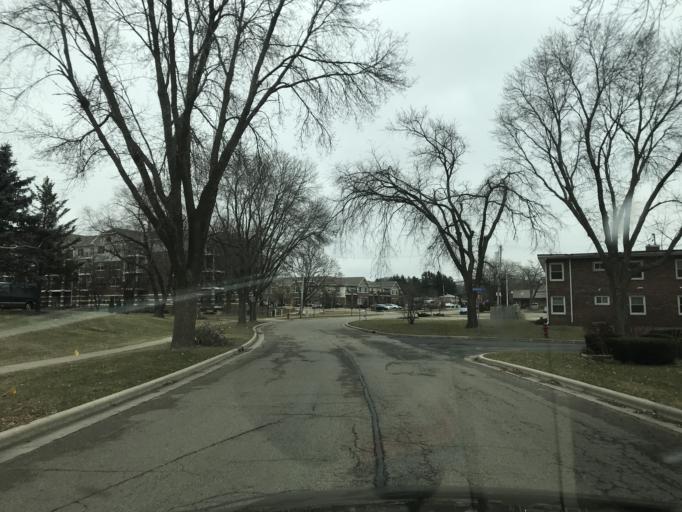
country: US
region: Wisconsin
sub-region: Dane County
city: Monona
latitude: 43.0567
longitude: -89.3293
